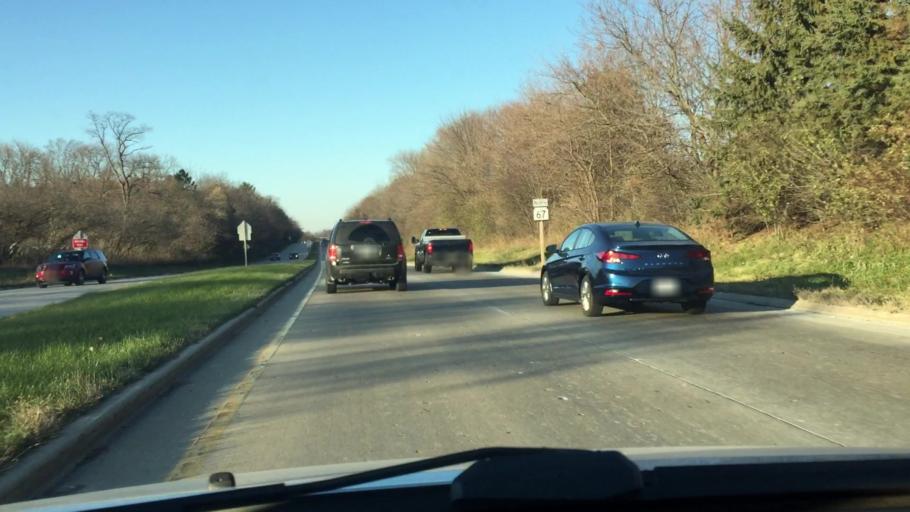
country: US
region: Wisconsin
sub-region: Waukesha County
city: Oconomowoc
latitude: 43.0974
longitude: -88.4802
